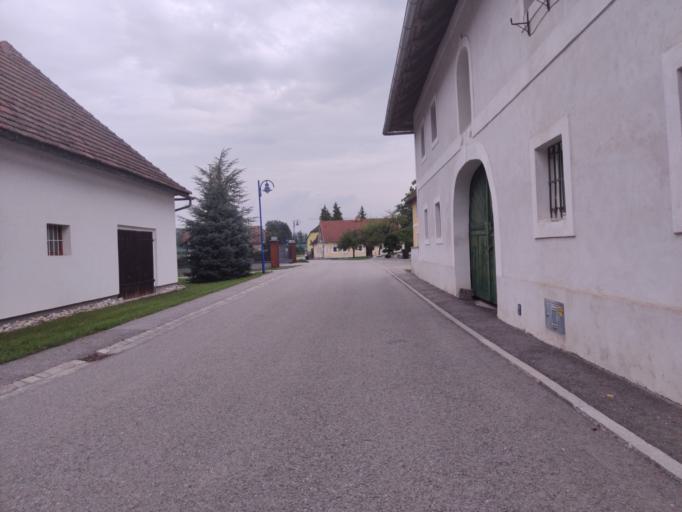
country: AT
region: Lower Austria
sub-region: Politischer Bezirk Amstetten
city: Ennsdorf
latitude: 48.2155
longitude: 14.4900
